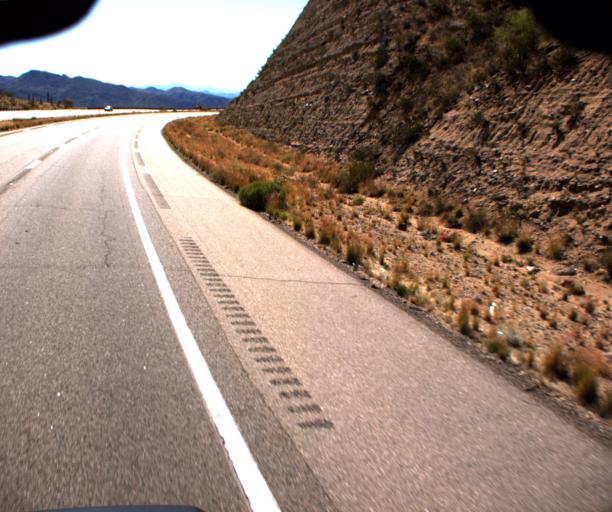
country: US
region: Arizona
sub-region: Yavapai County
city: Bagdad
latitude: 34.4476
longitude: -113.2776
